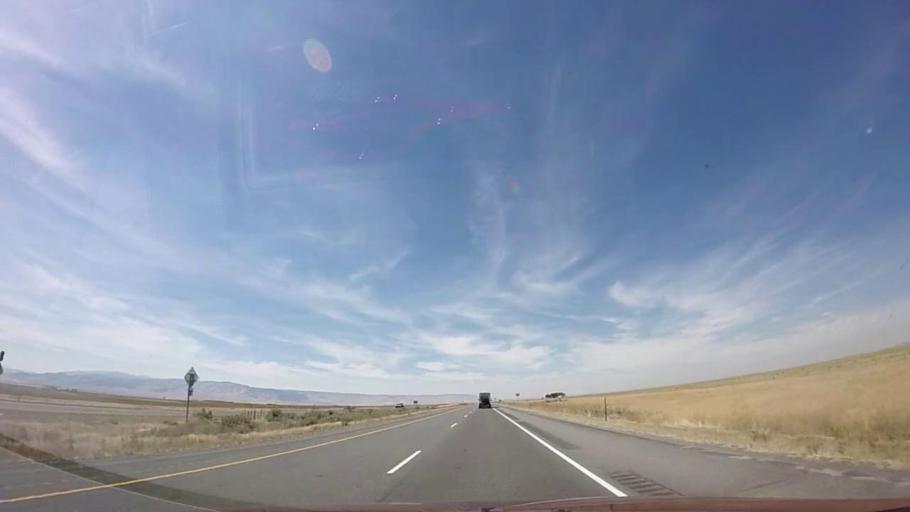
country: US
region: Idaho
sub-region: Minidoka County
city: Rupert
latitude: 42.3333
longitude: -113.2206
